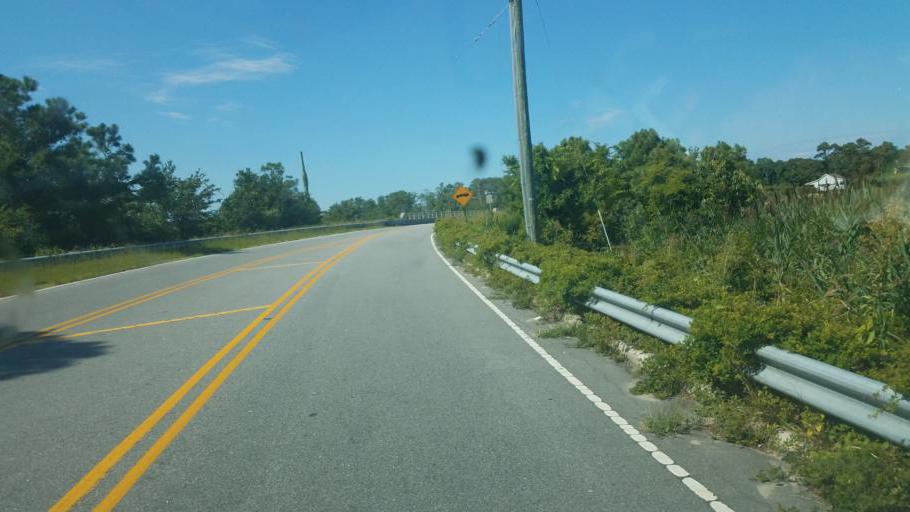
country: US
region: North Carolina
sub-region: Dare County
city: Kill Devil Hills
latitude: 36.0100
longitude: -75.6992
